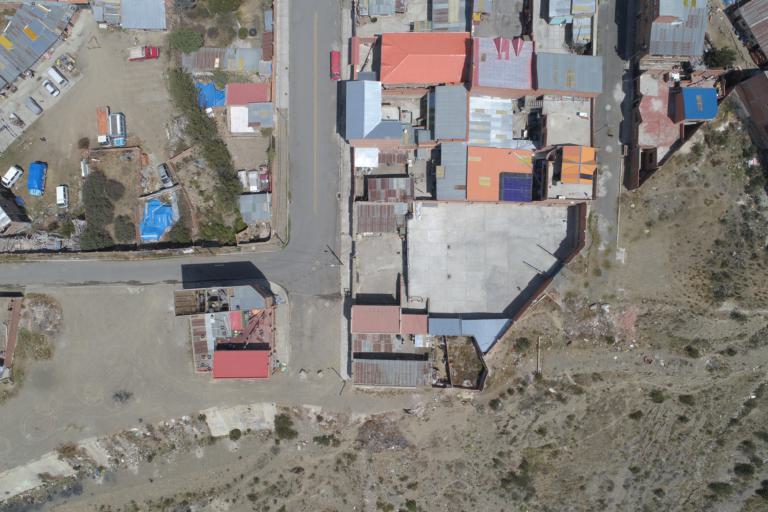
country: BO
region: La Paz
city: La Paz
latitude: -16.5040
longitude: -68.1011
